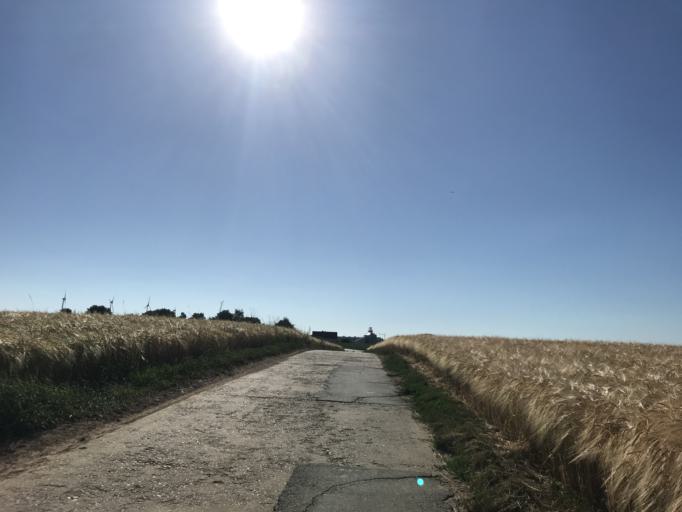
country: DE
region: Rheinland-Pfalz
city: Gau-Bischofsheim
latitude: 49.9434
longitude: 8.2753
